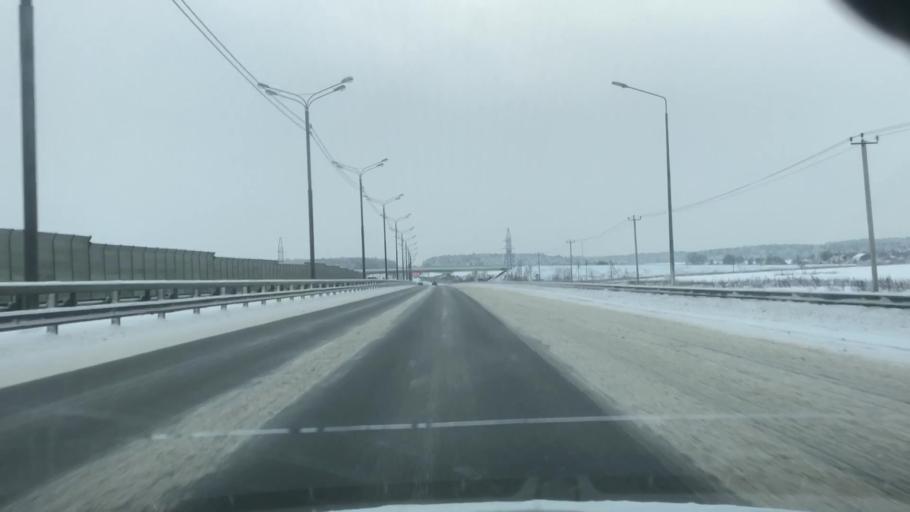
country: RU
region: Moskovskaya
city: Mikhnevo
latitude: 55.1901
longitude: 37.8961
